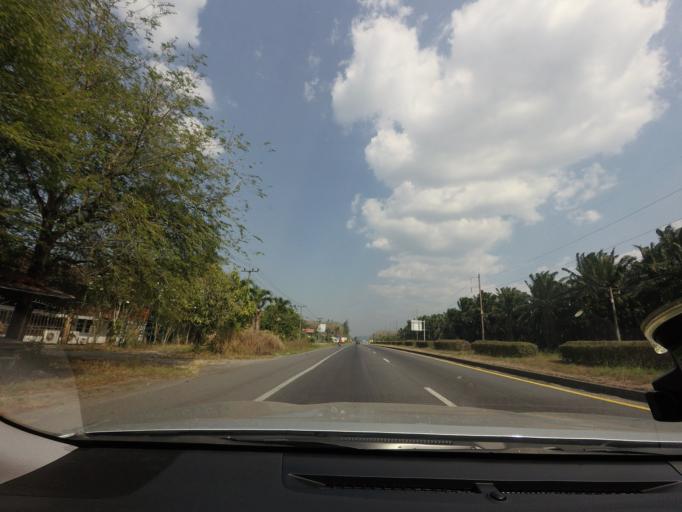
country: TH
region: Phangnga
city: Thap Put
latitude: 8.5092
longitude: 98.6518
